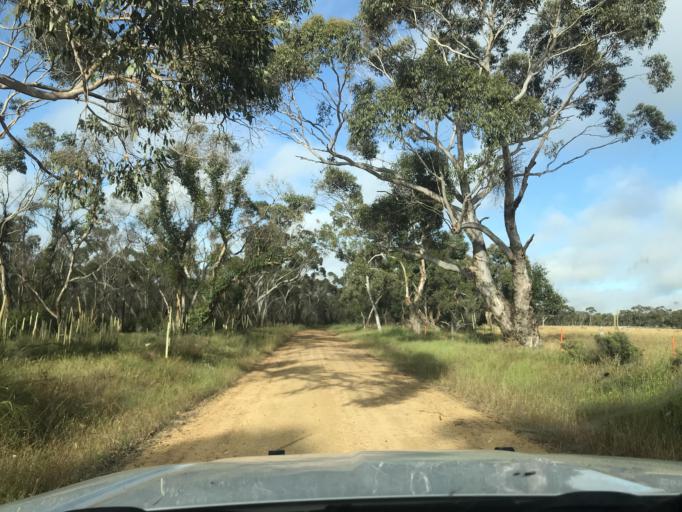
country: AU
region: South Australia
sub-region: Wattle Range
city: Penola
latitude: -37.1811
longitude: 141.1787
